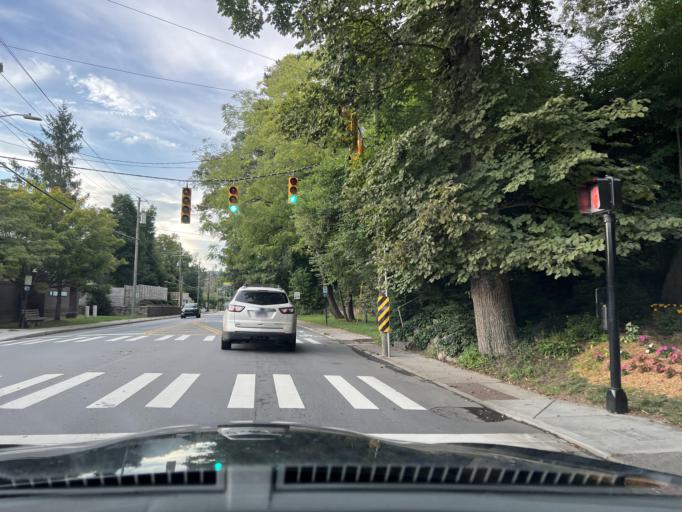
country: US
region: North Carolina
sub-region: Buncombe County
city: Asheville
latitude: 35.6070
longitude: -82.5462
